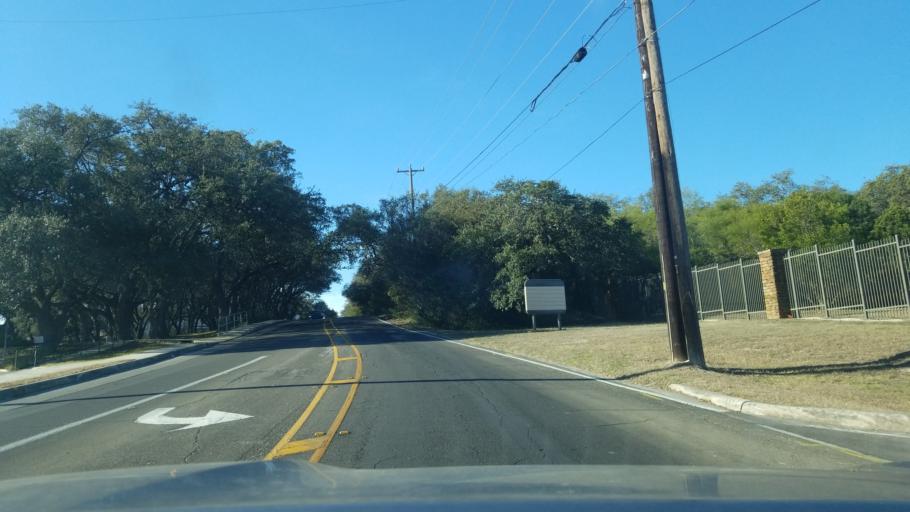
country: US
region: Texas
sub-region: Bexar County
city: Balcones Heights
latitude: 29.5328
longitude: -98.5682
